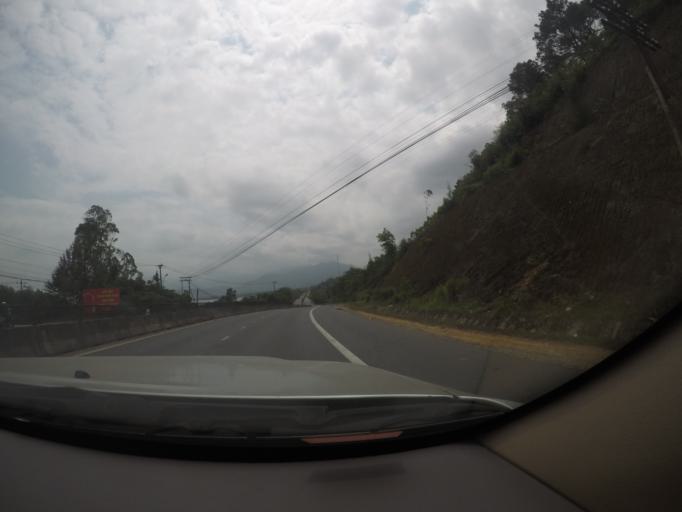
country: VN
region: Thua Thien-Hue
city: Phu Loc
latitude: 16.2879
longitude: 107.8543
